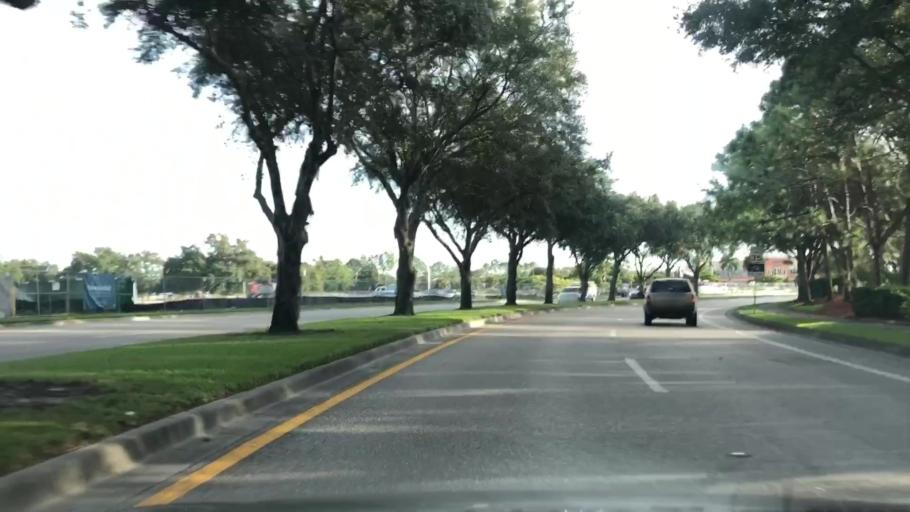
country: US
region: Florida
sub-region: Sarasota County
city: Fruitville
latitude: 27.3422
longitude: -82.4521
